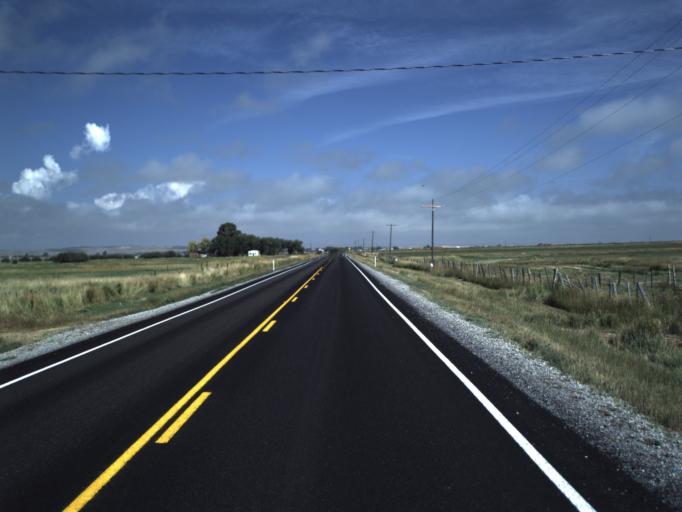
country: US
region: Utah
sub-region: Rich County
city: Randolph
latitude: 41.6293
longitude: -111.1791
